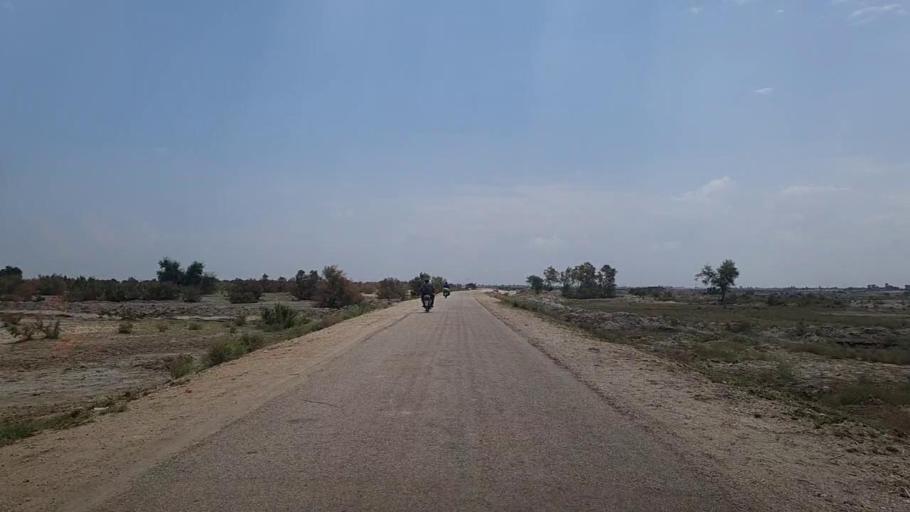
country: PK
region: Sindh
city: Kandhkot
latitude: 28.2898
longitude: 69.1464
